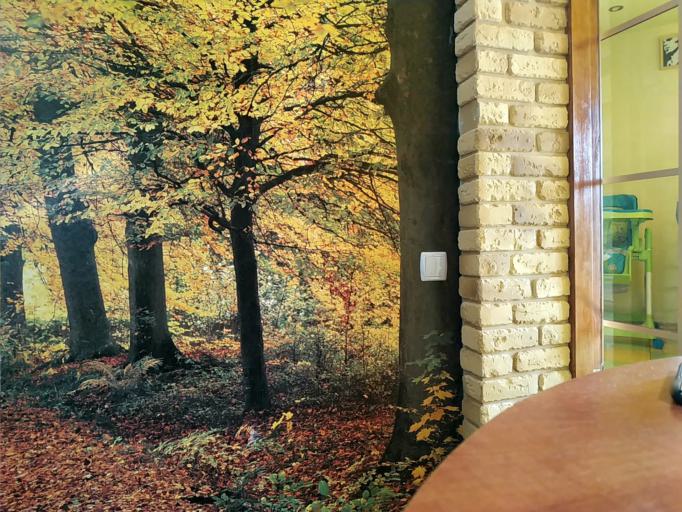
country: RU
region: Novgorod
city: Parfino
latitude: 57.8013
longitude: 31.6088
